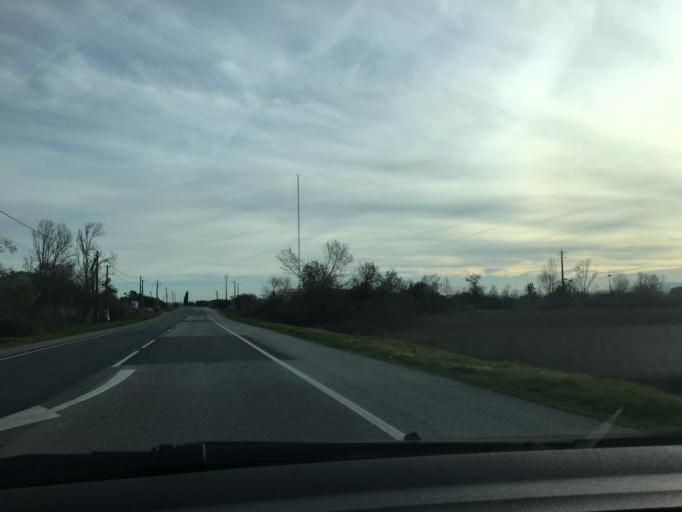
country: PT
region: Coimbra
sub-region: Soure
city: Alfarelos
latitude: 40.2014
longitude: -8.6397
